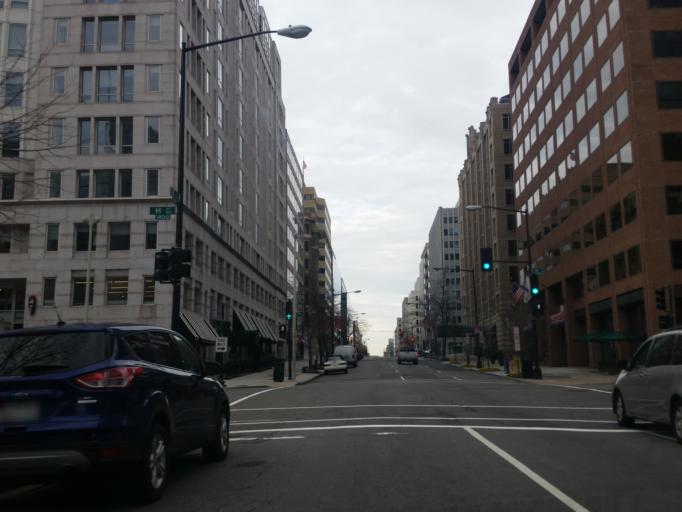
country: US
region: Washington, D.C.
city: Washington, D.C.
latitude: 38.8999
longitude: -77.0417
